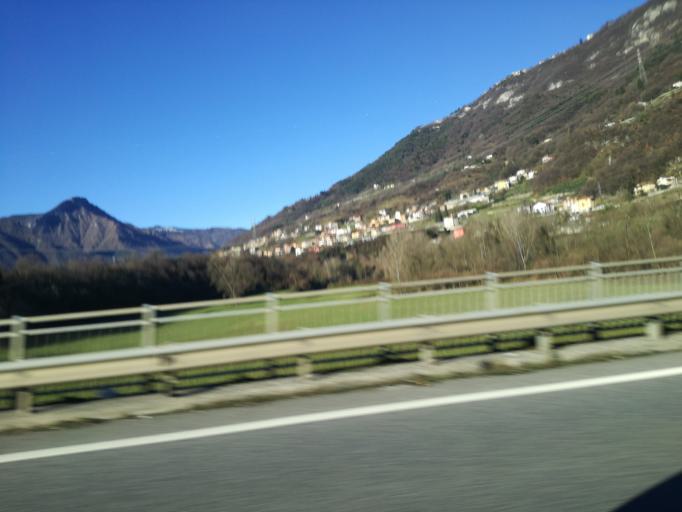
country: IT
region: Lombardy
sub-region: Provincia di Bergamo
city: Pianico
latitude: 45.8108
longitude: 10.0553
